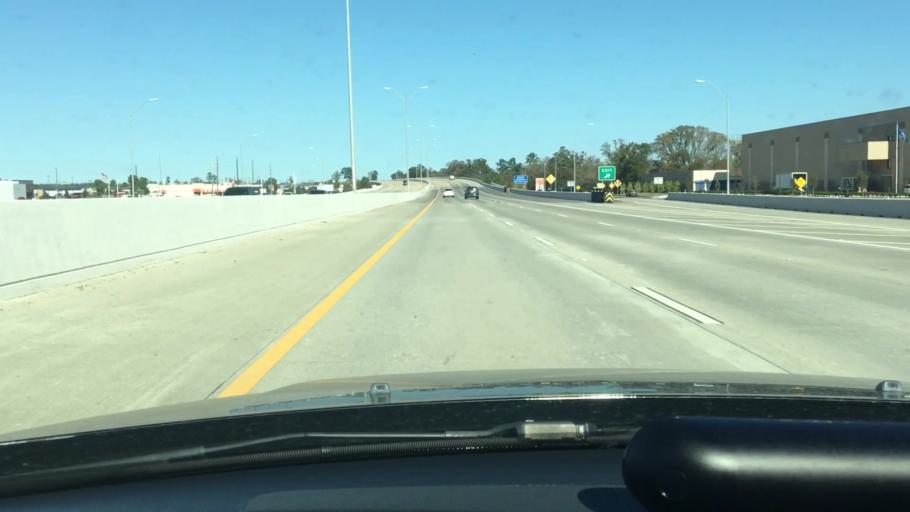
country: US
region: Texas
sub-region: Harris County
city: Atascocita
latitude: 29.9196
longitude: -95.2003
